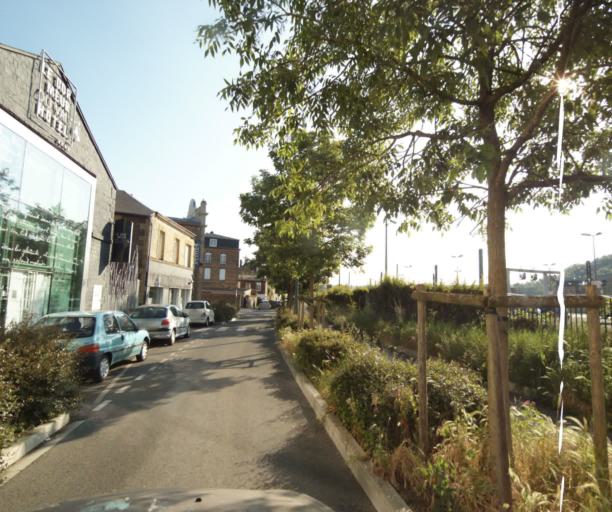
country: FR
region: Champagne-Ardenne
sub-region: Departement des Ardennes
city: Charleville-Mezieres
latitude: 49.7697
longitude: 4.7254
